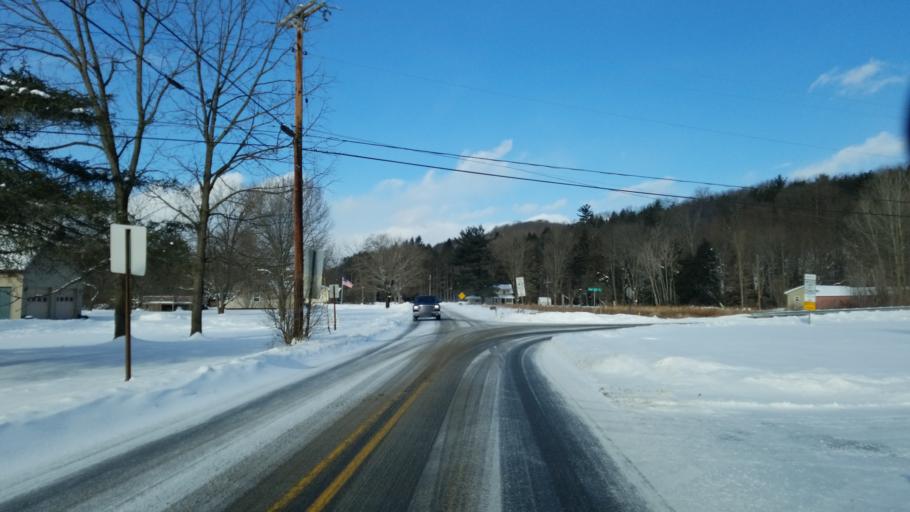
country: US
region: Pennsylvania
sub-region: Clearfield County
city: Hyde
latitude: 41.0127
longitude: -78.4717
